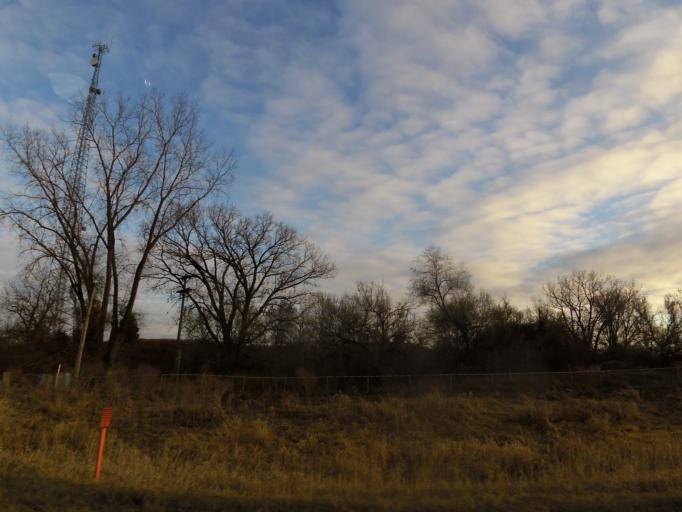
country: US
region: Minnesota
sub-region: Ramsey County
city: New Brighton
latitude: 45.0665
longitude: -93.1838
